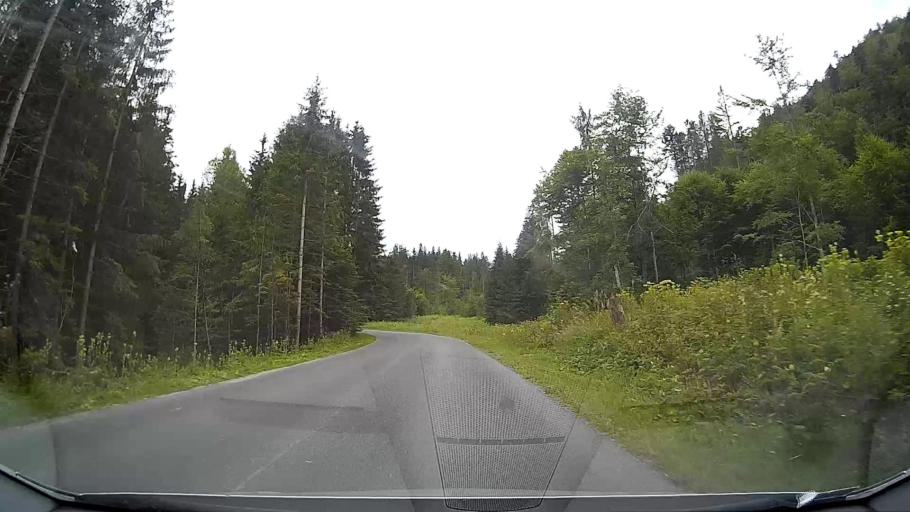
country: SK
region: Banskobystricky
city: Revuca
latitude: 48.8016
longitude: 20.1450
